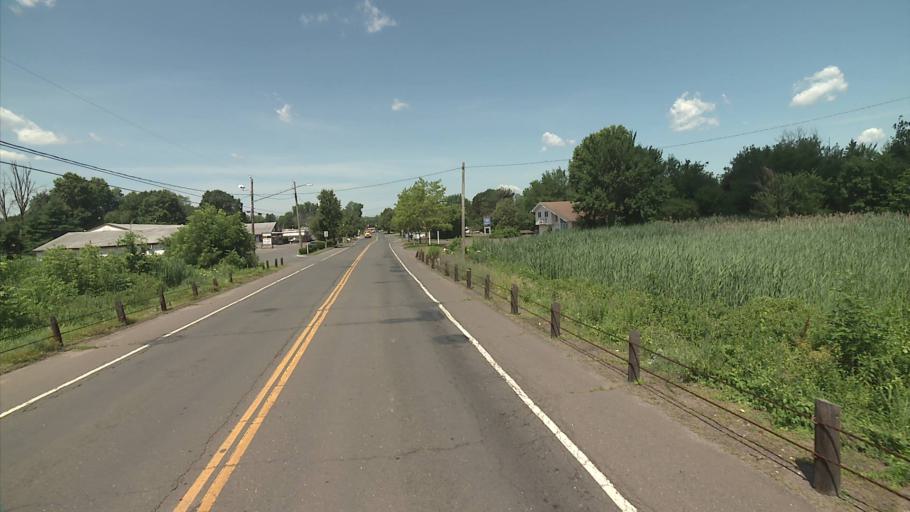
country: US
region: Connecticut
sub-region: Hartford County
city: Kensington
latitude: 41.6257
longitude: -72.7467
